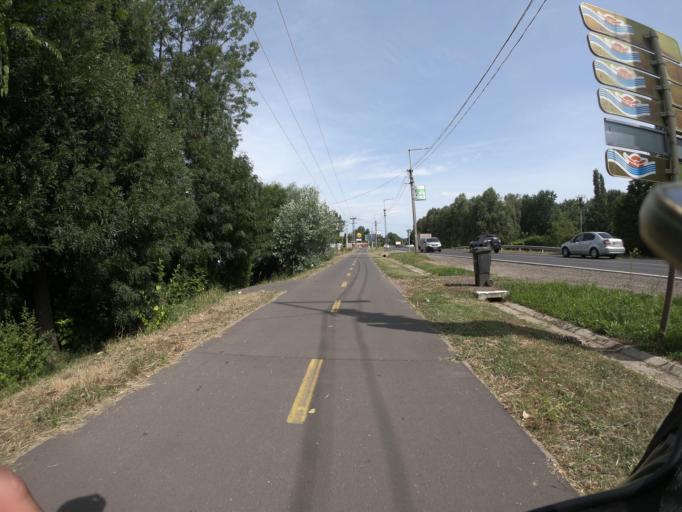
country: HU
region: Jasz-Nagykun-Szolnok
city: Tiszafured
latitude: 47.6222
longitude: 20.7475
